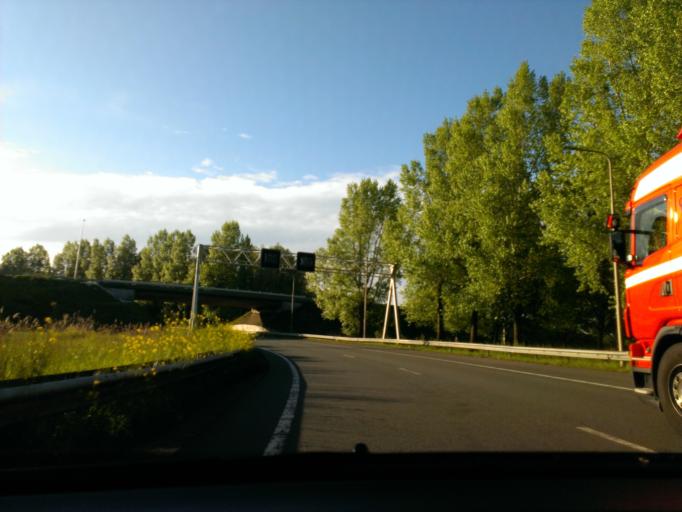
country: NL
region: South Holland
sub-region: Gemeente Ridderkerk
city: Ridderkerk
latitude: 51.8749
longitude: 4.5774
